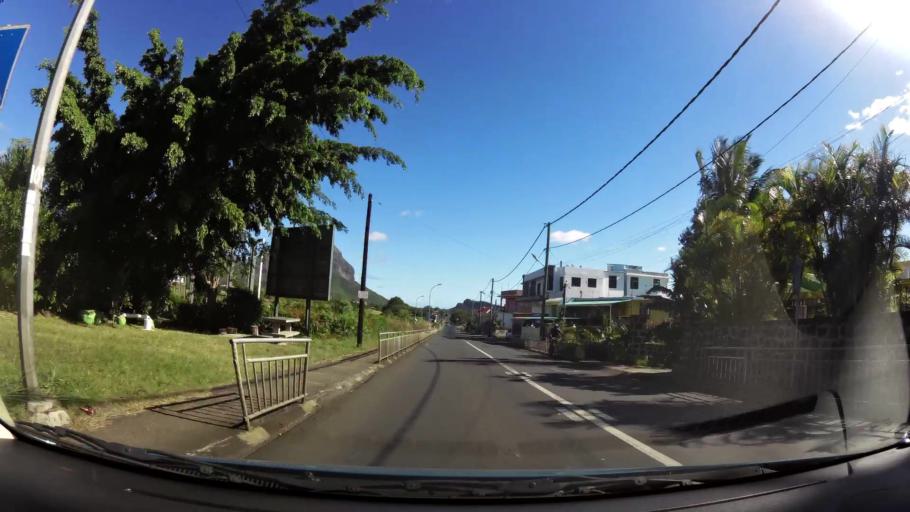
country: MU
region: Plaines Wilhems
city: Vacoas
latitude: -20.2812
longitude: 57.4539
